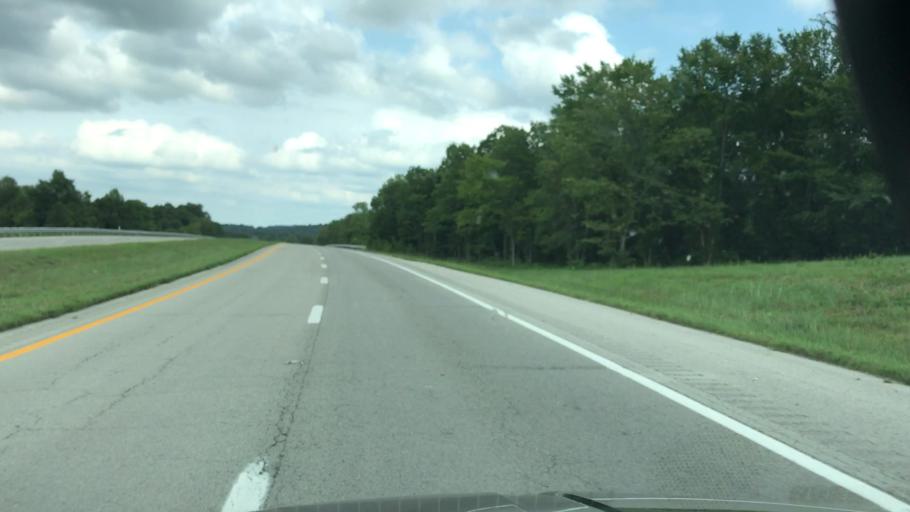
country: US
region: Kentucky
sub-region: Caldwell County
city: Princeton
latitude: 37.1403
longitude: -87.8144
